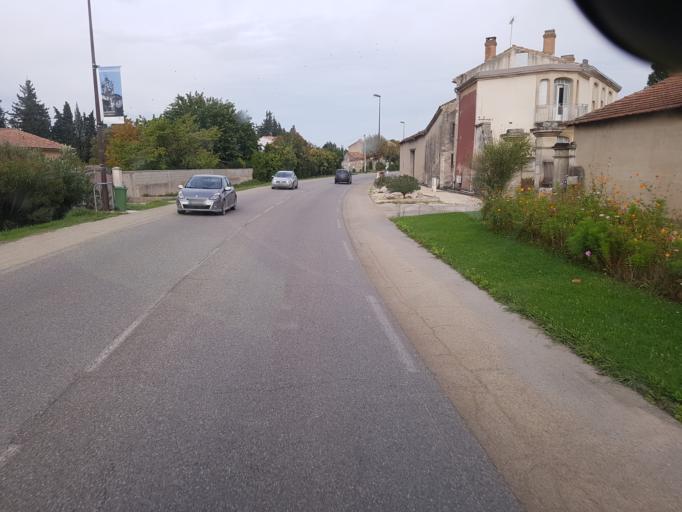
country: FR
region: Provence-Alpes-Cote d'Azur
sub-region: Departement des Bouches-du-Rhone
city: Barbentane
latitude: 43.9038
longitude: 4.7572
